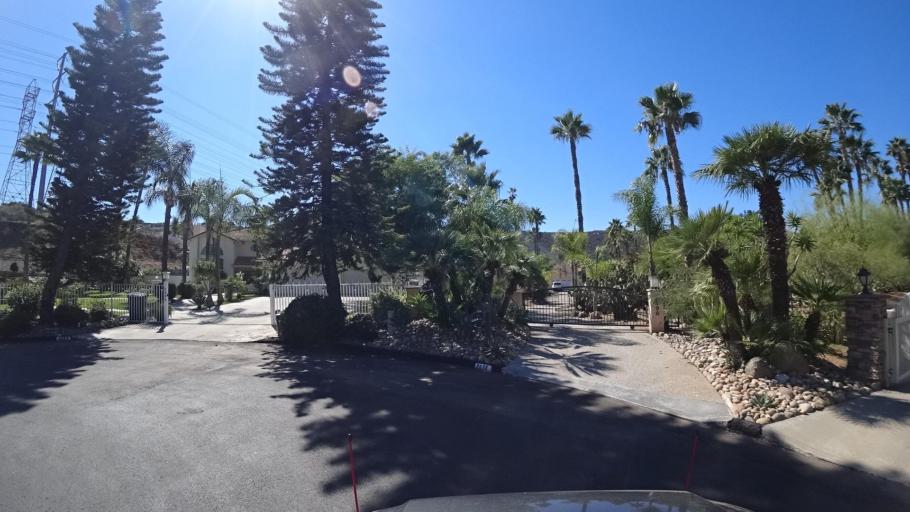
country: US
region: California
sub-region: San Diego County
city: Rancho San Diego
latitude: 32.7384
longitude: -116.9158
